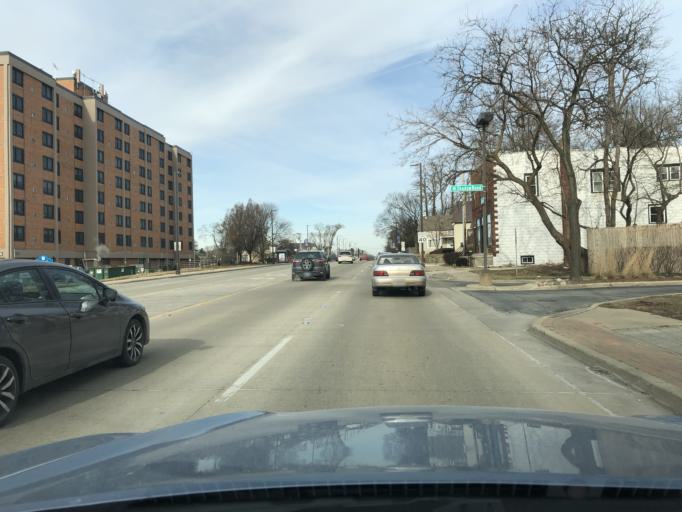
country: US
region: Illinois
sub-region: Cook County
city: Wheeling
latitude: 42.1428
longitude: -87.9091
